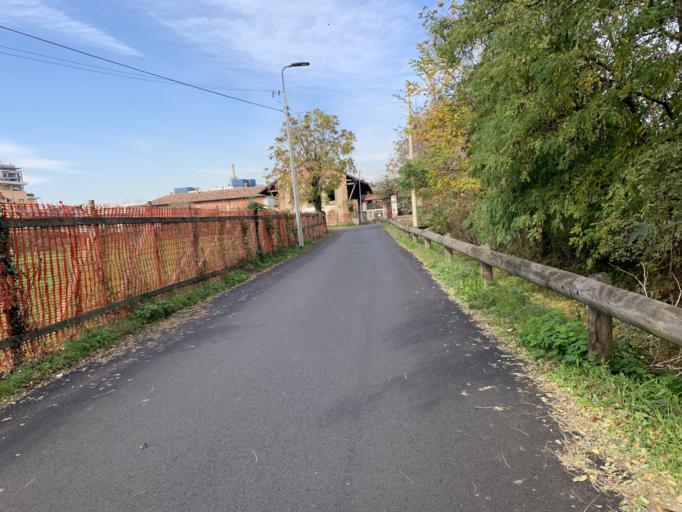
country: IT
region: Lombardy
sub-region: Citta metropolitana di Milano
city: Chiaravalle
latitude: 45.4338
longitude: 9.2095
